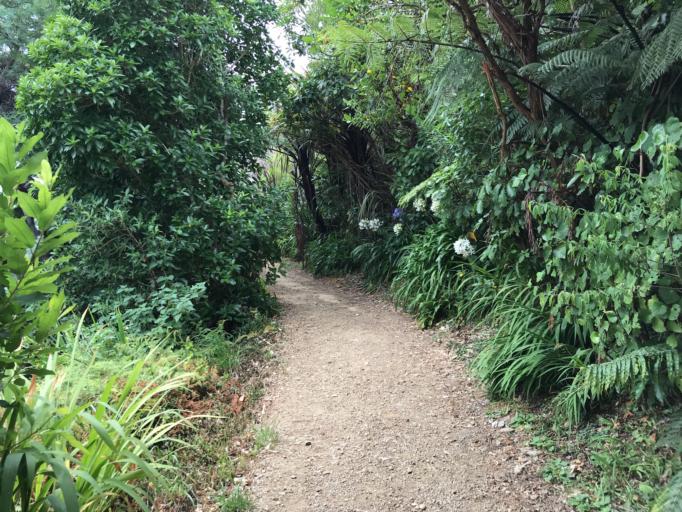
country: NZ
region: Marlborough
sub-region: Marlborough District
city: Picton
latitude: -41.1006
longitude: 174.1845
